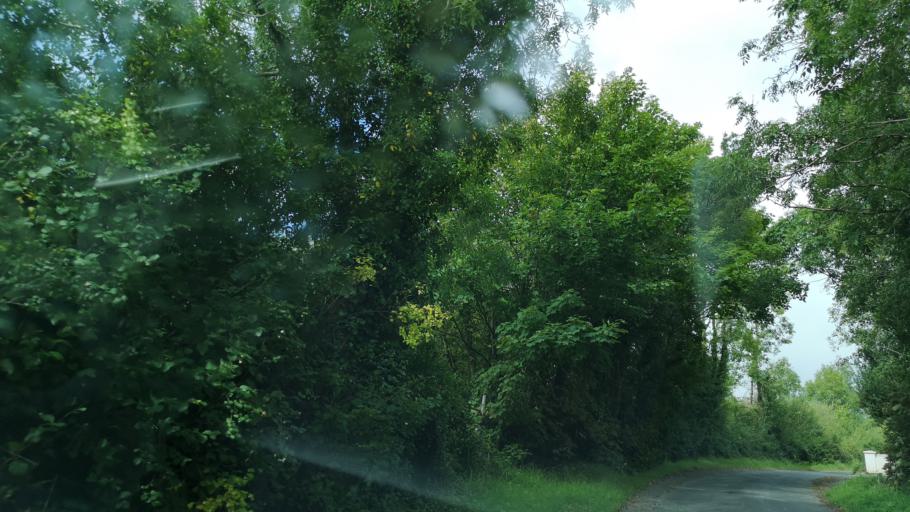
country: IE
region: Connaught
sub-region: County Galway
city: Loughrea
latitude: 53.3034
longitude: -8.6044
